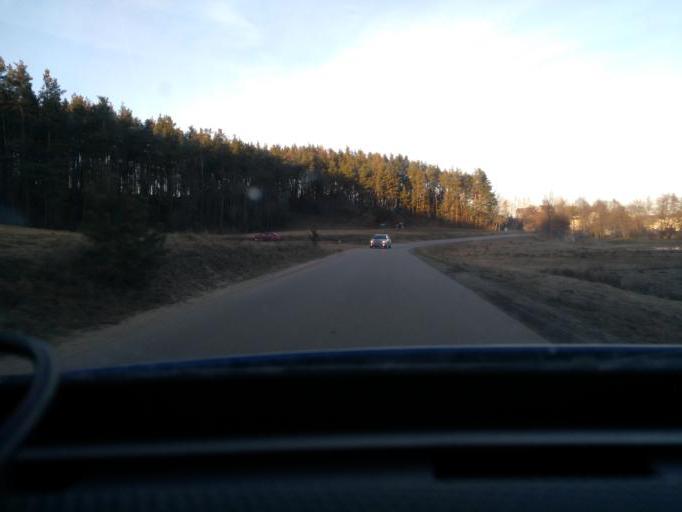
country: PL
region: Pomeranian Voivodeship
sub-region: Powiat kartuski
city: Przodkowo
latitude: 54.3813
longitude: 18.2663
